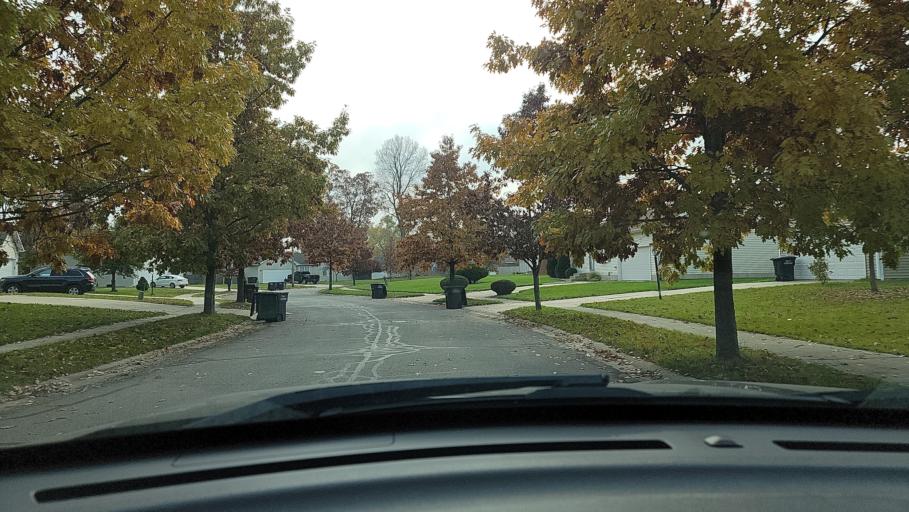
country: US
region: Indiana
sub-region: Porter County
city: Portage
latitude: 41.5885
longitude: -87.1681
